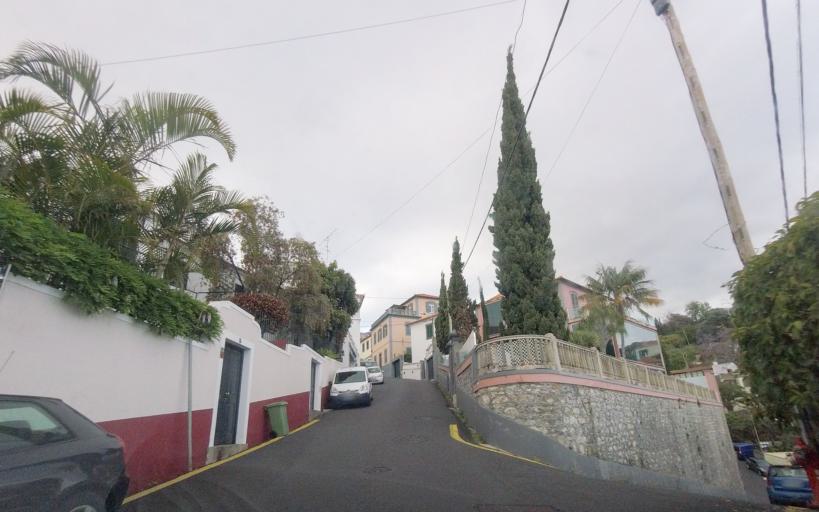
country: PT
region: Madeira
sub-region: Funchal
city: Nossa Senhora do Monte
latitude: 32.6525
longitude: -16.8982
